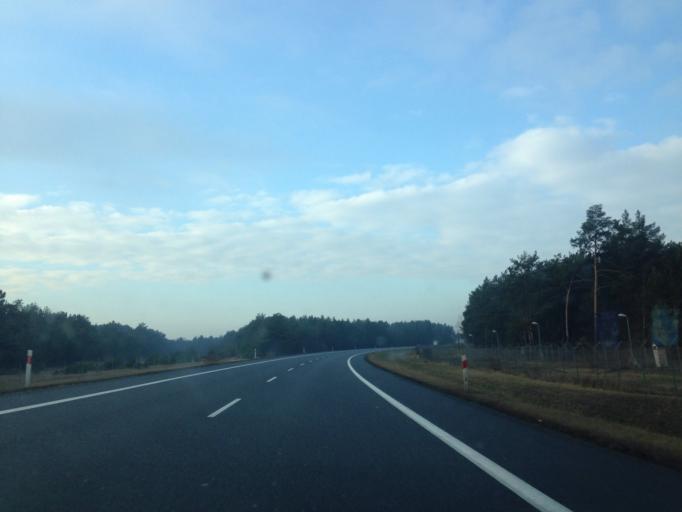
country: PL
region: Kujawsko-Pomorskie
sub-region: Torun
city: Torun
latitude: 52.9759
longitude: 18.6237
